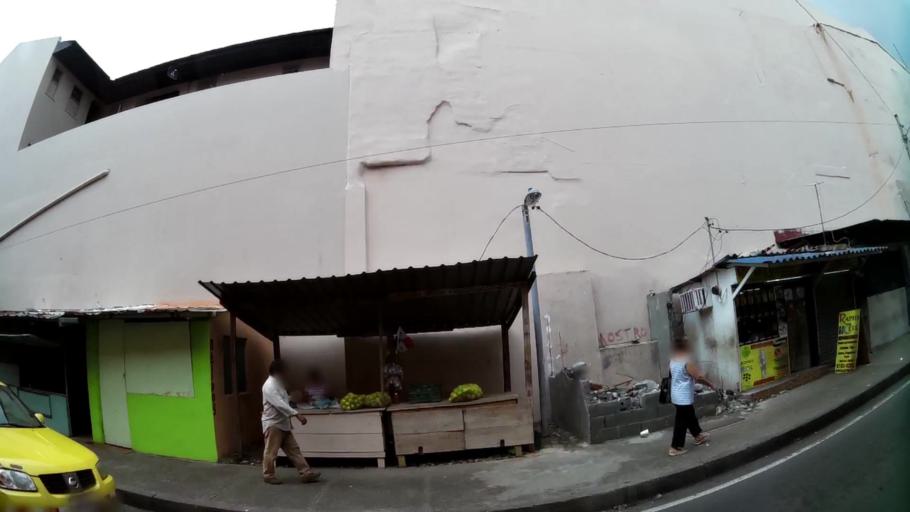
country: PA
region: Panama
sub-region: Distrito de Panama
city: Ancon
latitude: 8.9576
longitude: -79.5403
